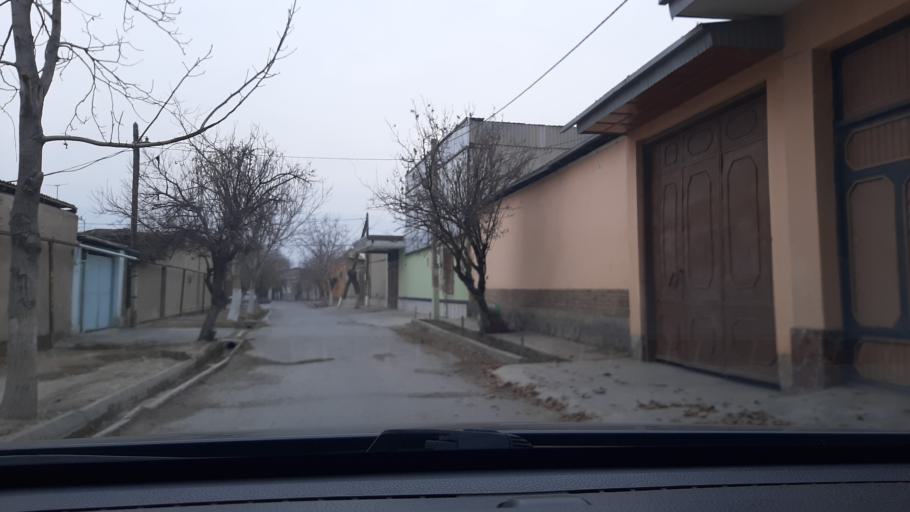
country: TJ
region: Viloyati Sughd
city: Khujand
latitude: 40.2652
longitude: 69.6155
